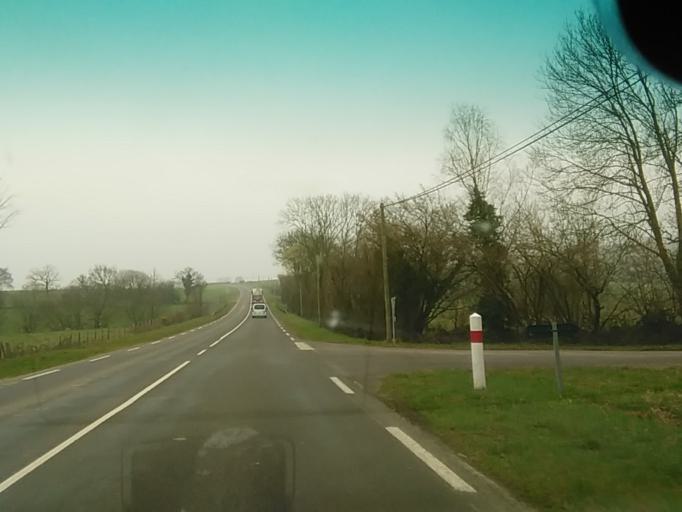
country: FR
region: Lower Normandy
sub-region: Departement de l'Orne
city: Magny-le-Desert
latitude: 48.6292
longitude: -0.2520
